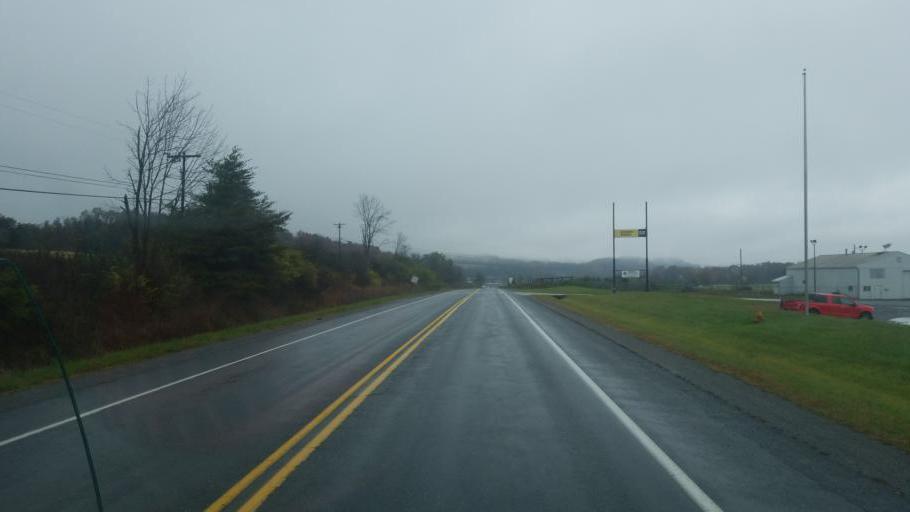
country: US
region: Pennsylvania
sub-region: Centre County
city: Milesburg
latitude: 40.9619
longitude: -77.7611
